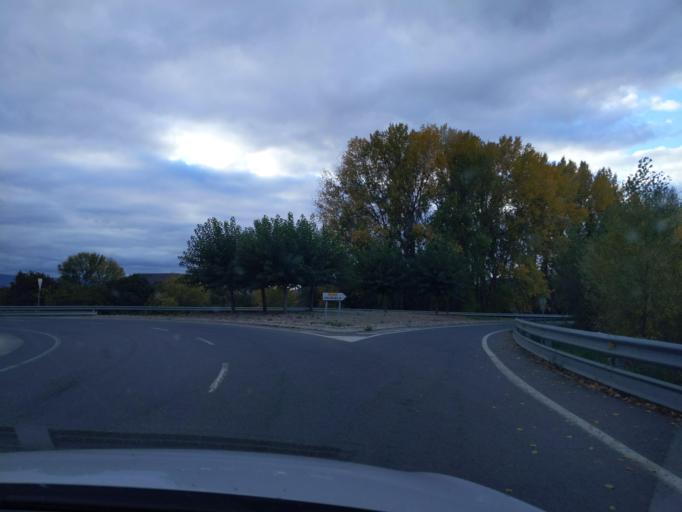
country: ES
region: La Rioja
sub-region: Provincia de La Rioja
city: Urunuela
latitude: 42.4393
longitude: -2.7048
